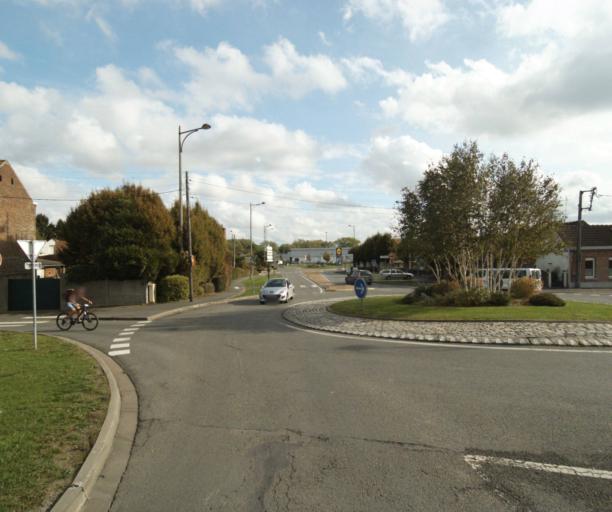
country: FR
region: Nord-Pas-de-Calais
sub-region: Departement du Nord
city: Wavrin
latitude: 50.5669
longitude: 2.9280
